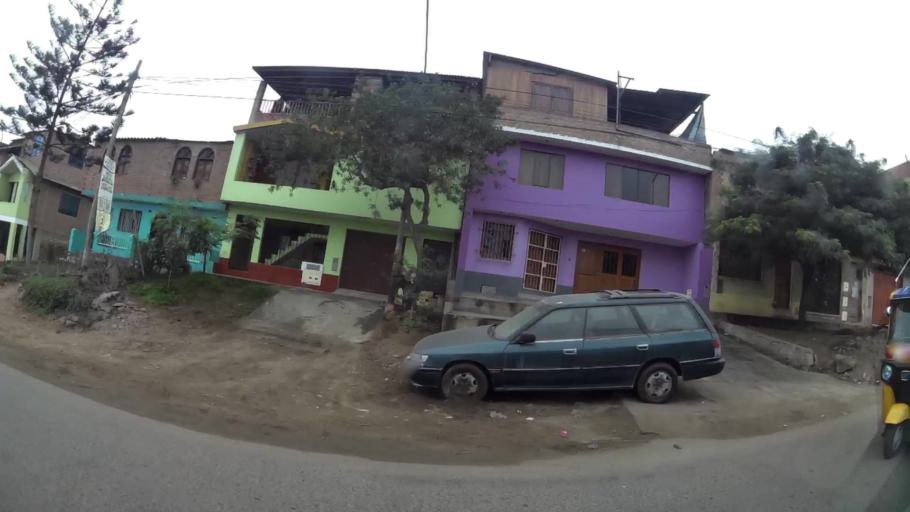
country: PE
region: Lima
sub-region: Lima
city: Surco
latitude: -12.1687
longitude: -76.9565
